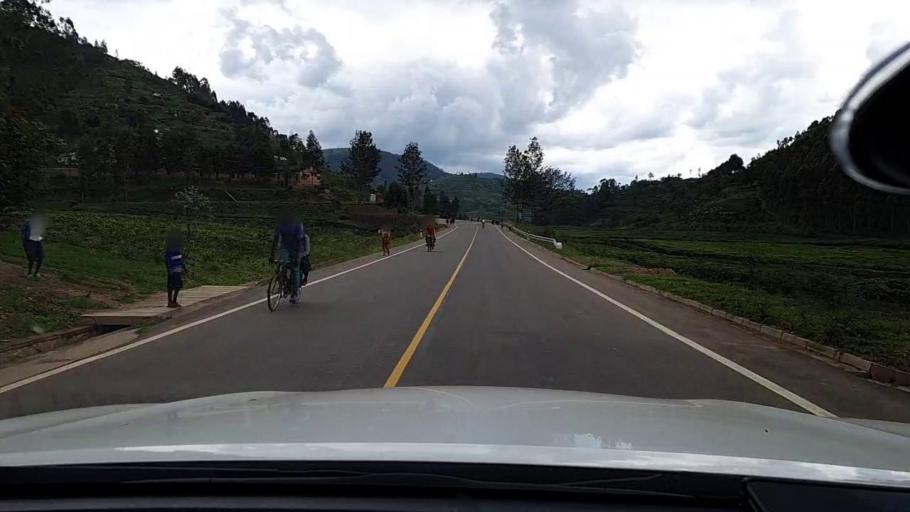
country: RW
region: Northern Province
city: Byumba
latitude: -1.6543
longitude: 29.9113
